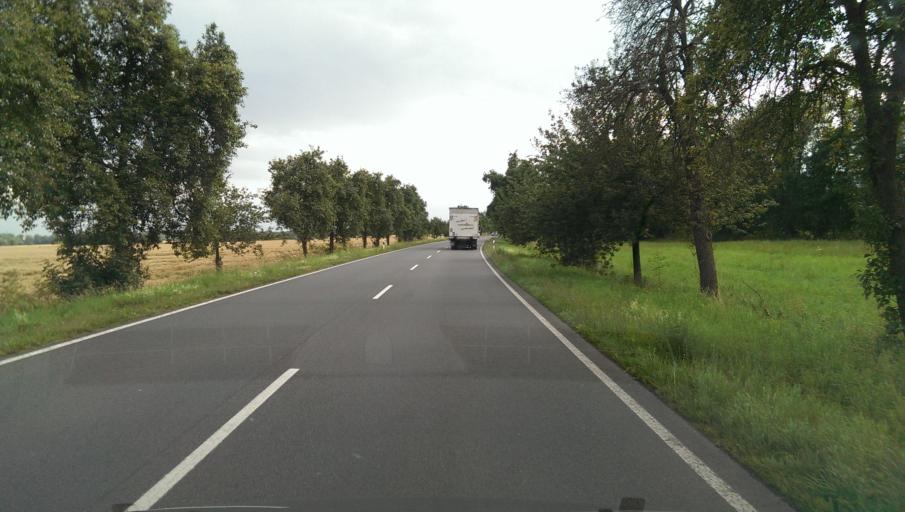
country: DE
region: Saxony
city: Elstertrebnitz
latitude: 51.1501
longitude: 12.2466
